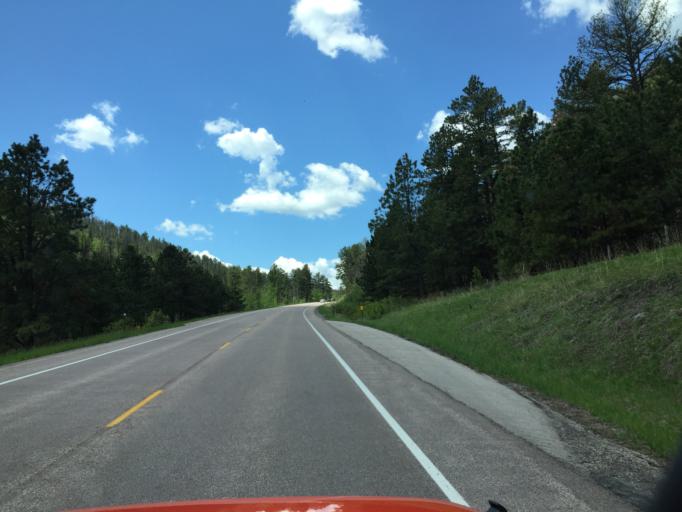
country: US
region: South Dakota
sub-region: Custer County
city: Custer
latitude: 43.8948
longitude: -103.5600
